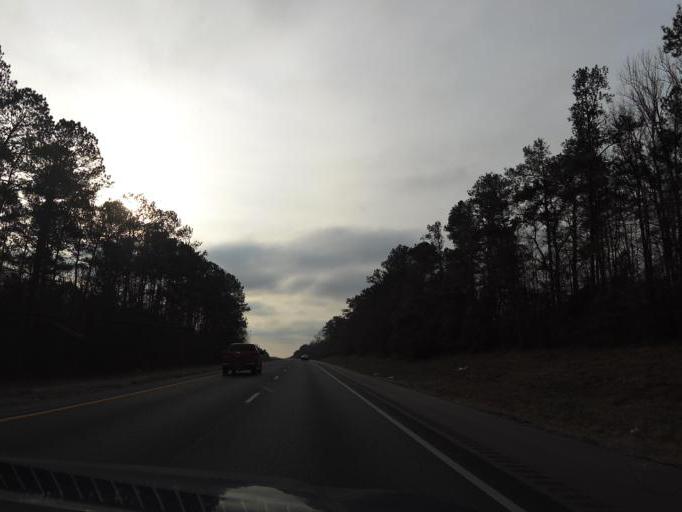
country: US
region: Alabama
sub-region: Chilton County
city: Clanton
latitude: 32.7721
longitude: -86.5675
